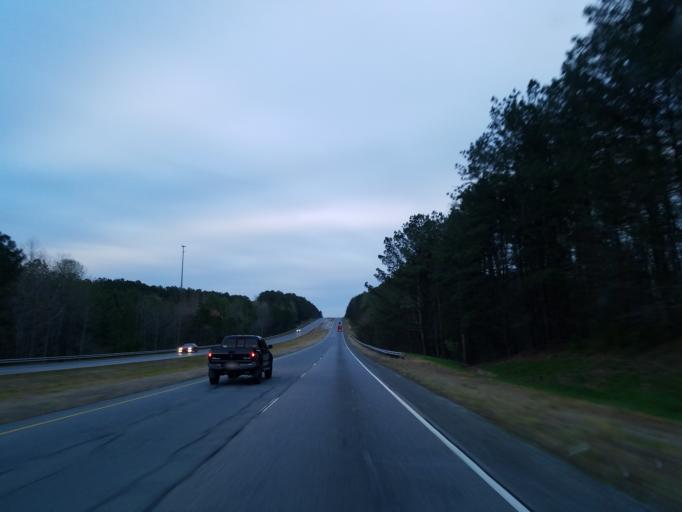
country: US
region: Georgia
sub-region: Pickens County
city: Jasper
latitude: 34.4970
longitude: -84.4958
